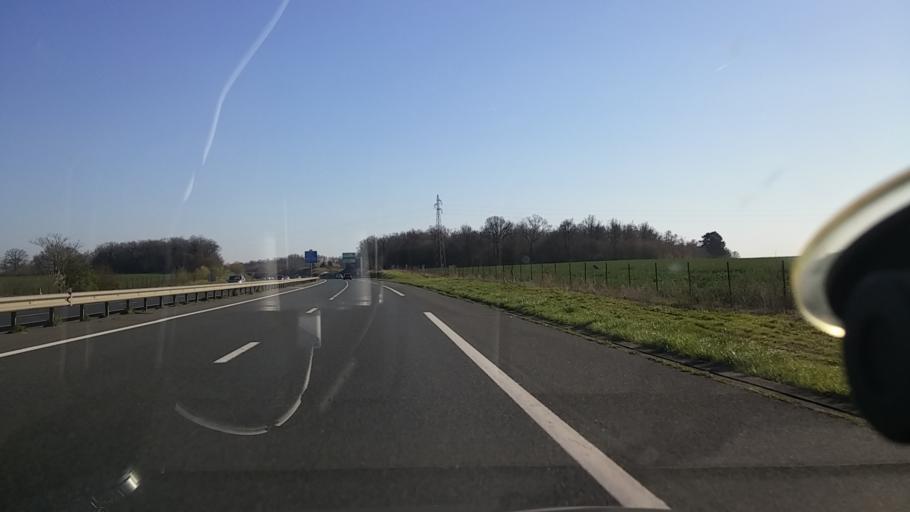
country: FR
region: Centre
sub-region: Departement de l'Indre
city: Saint-Maur
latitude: 46.8016
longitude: 1.6162
